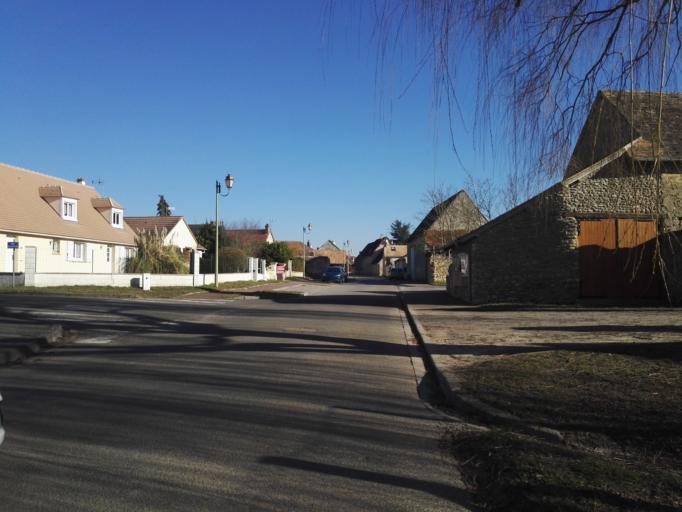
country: FR
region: Haute-Normandie
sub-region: Departement de l'Eure
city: Pacy-sur-Eure
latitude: 49.0067
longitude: 1.4195
